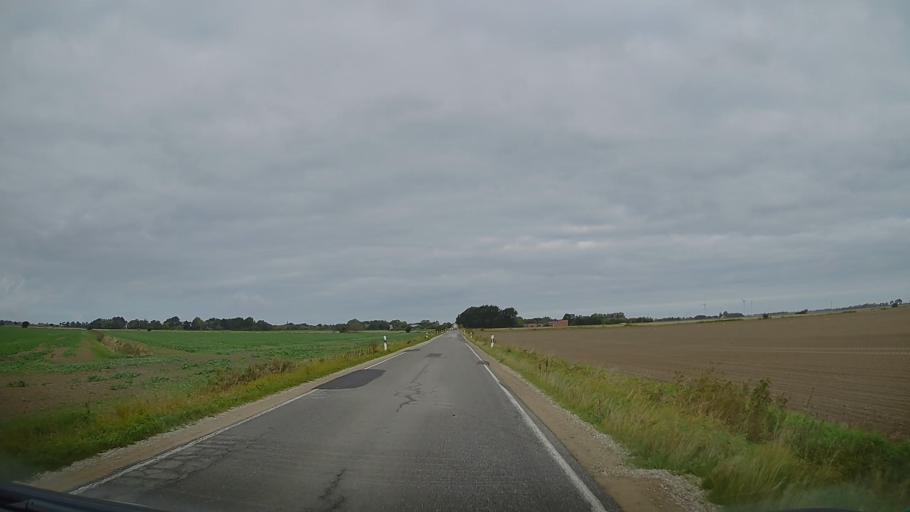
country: DE
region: Schleswig-Holstein
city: Emmelsbull-Horsbull
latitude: 54.8030
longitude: 8.7126
